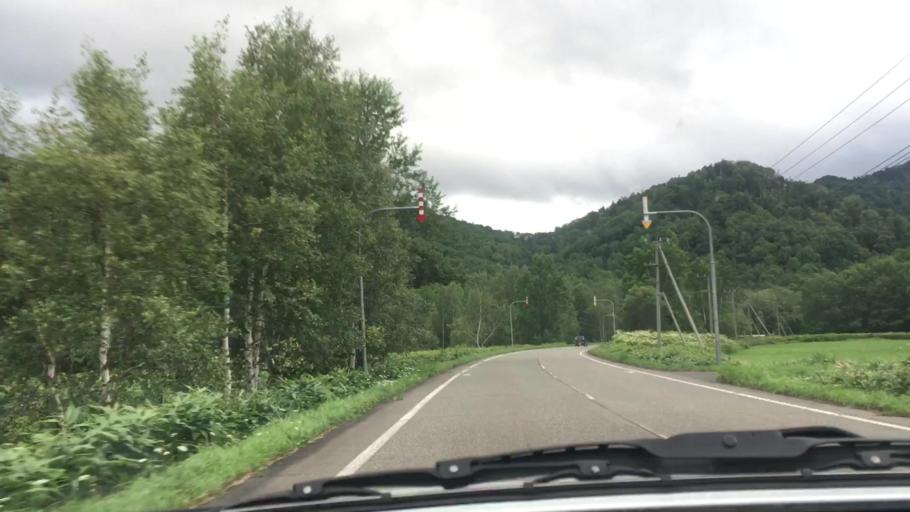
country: JP
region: Hokkaido
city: Shimo-furano
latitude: 43.0470
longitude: 142.5326
